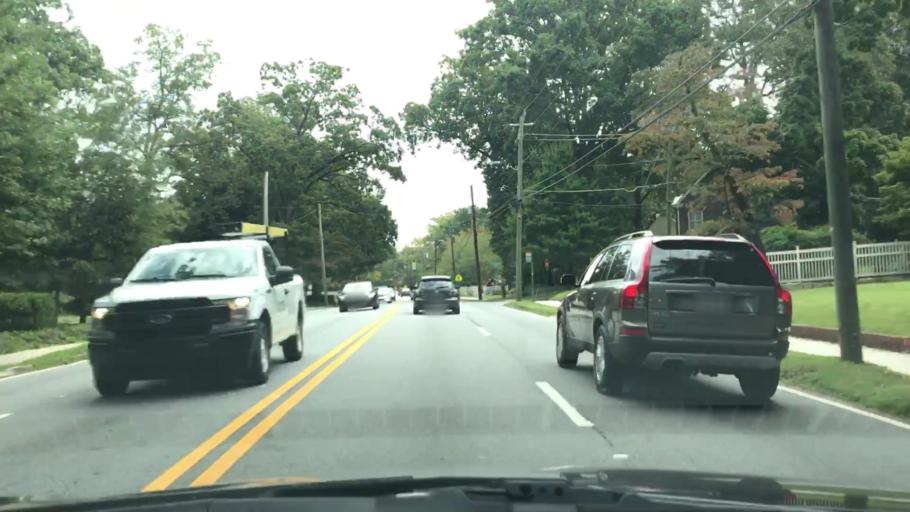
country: US
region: Georgia
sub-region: DeKalb County
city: North Decatur
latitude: 33.7838
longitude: -84.3025
